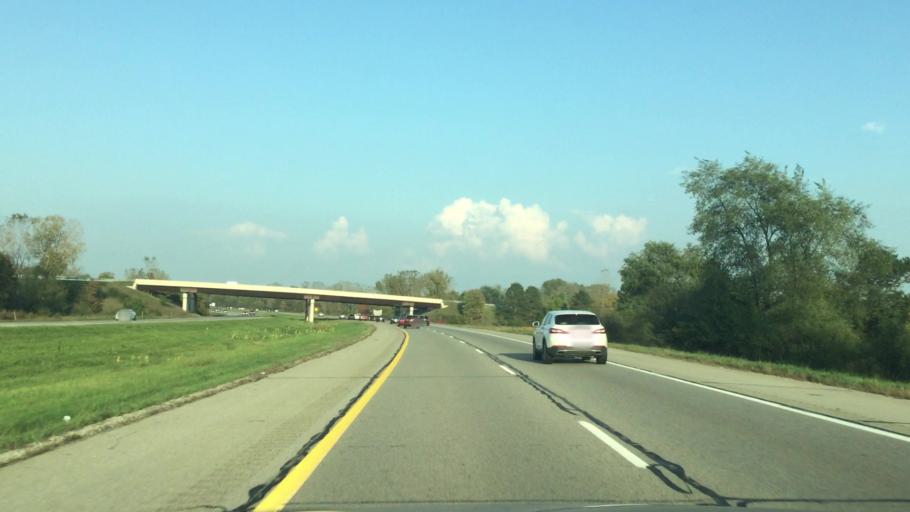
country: US
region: Michigan
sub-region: Washtenaw County
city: Ypsilanti
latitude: 42.3261
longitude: -83.6355
